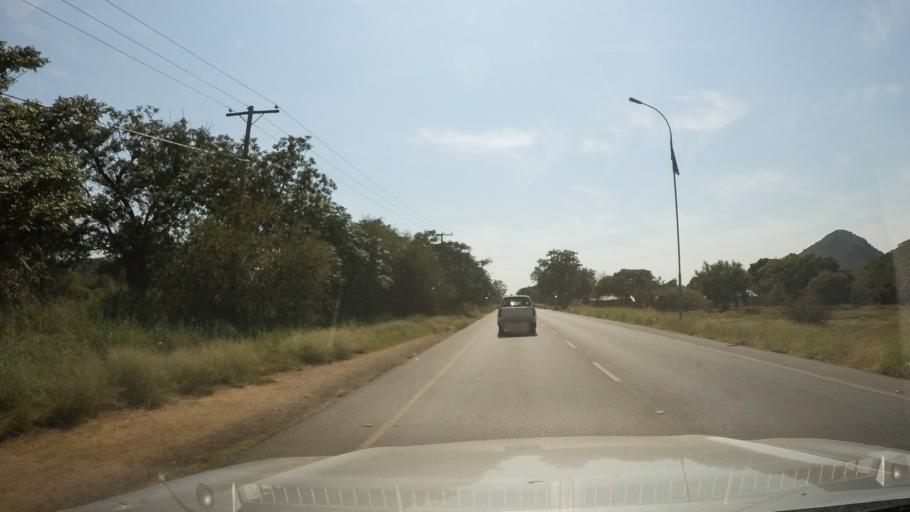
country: BW
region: South East
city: Lobatse
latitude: -25.2208
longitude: 25.6797
